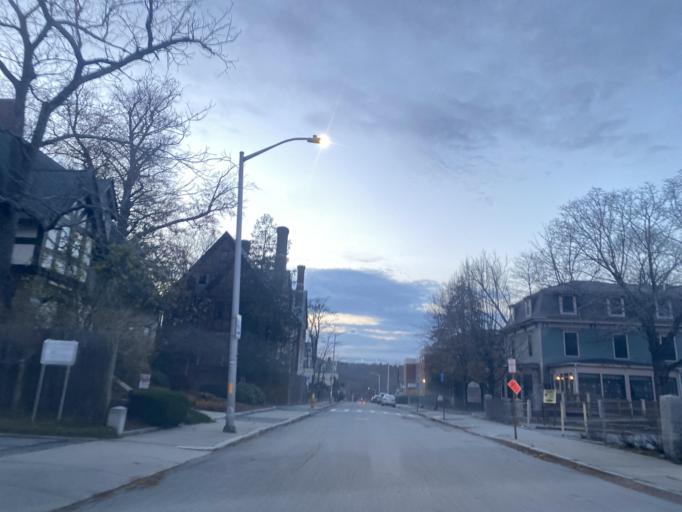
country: US
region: Massachusetts
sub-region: Worcester County
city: Worcester
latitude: 42.2663
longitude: -71.8060
